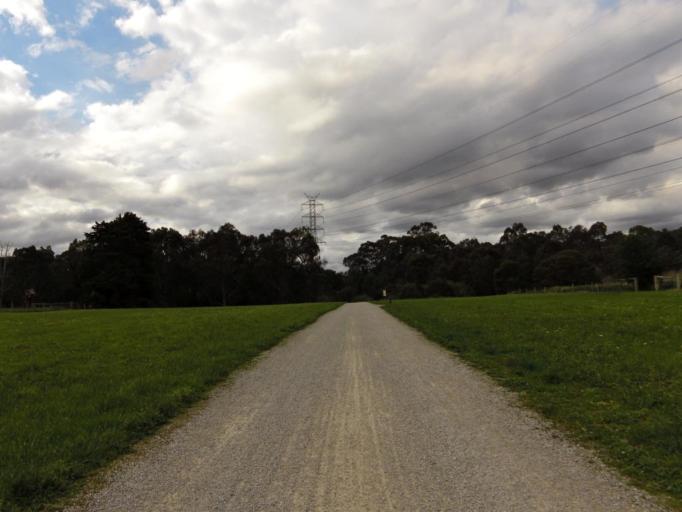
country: AU
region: Victoria
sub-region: Manningham
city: Bulleen
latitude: -37.7704
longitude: 145.0713
